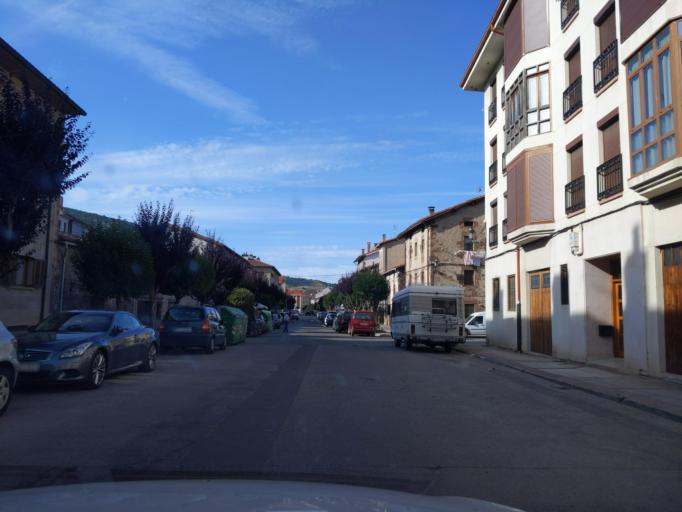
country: ES
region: La Rioja
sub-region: Provincia de La Rioja
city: Ezcaray
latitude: 42.3248
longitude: -3.0122
